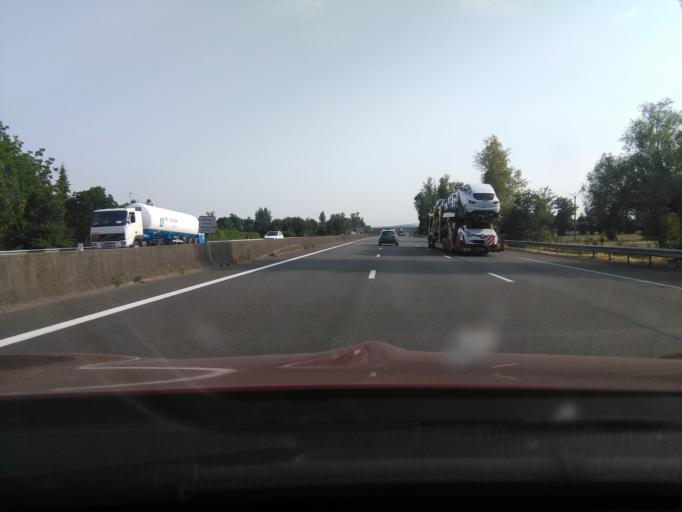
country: FR
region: Rhone-Alpes
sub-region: Departement du Rhone
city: Saint-Georges-de-Reneins
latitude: 46.0707
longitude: 4.7406
